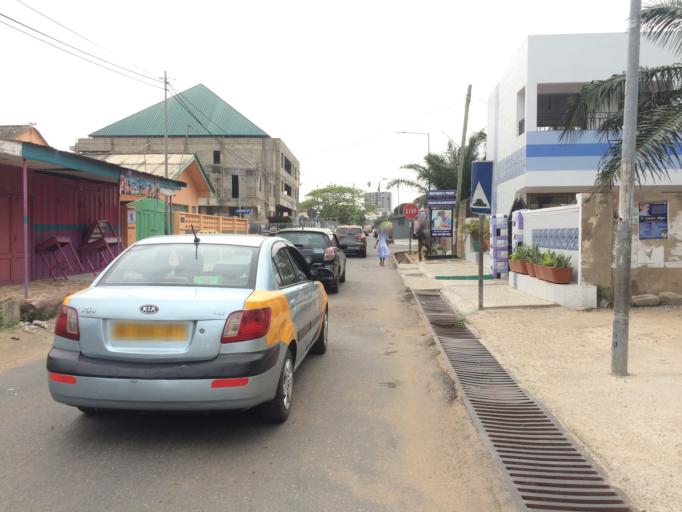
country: GH
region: Greater Accra
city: Accra
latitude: 5.5536
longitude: -0.1800
